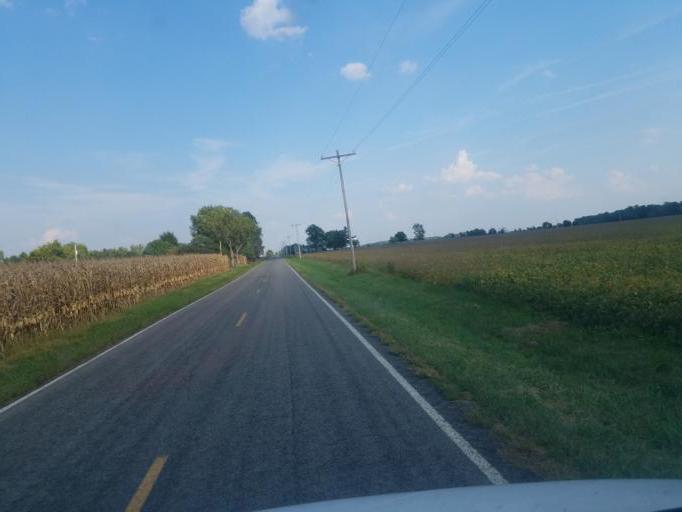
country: US
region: Ohio
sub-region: Hardin County
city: Forest
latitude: 40.9050
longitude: -83.5068
